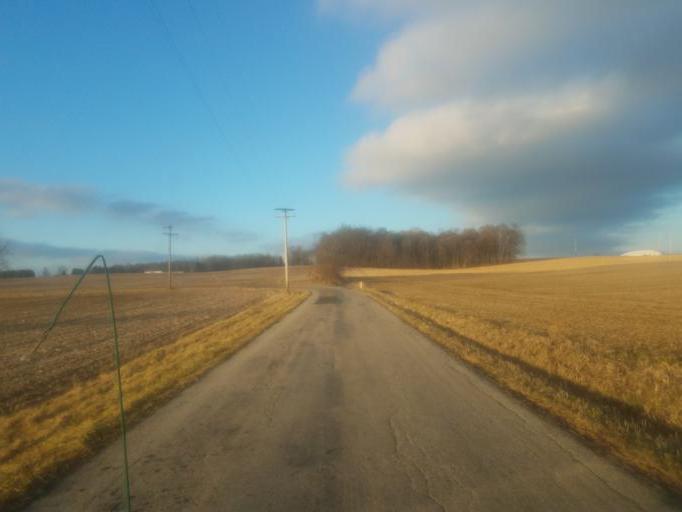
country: US
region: Ohio
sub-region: Knox County
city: Fredericktown
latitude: 40.5434
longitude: -82.5283
